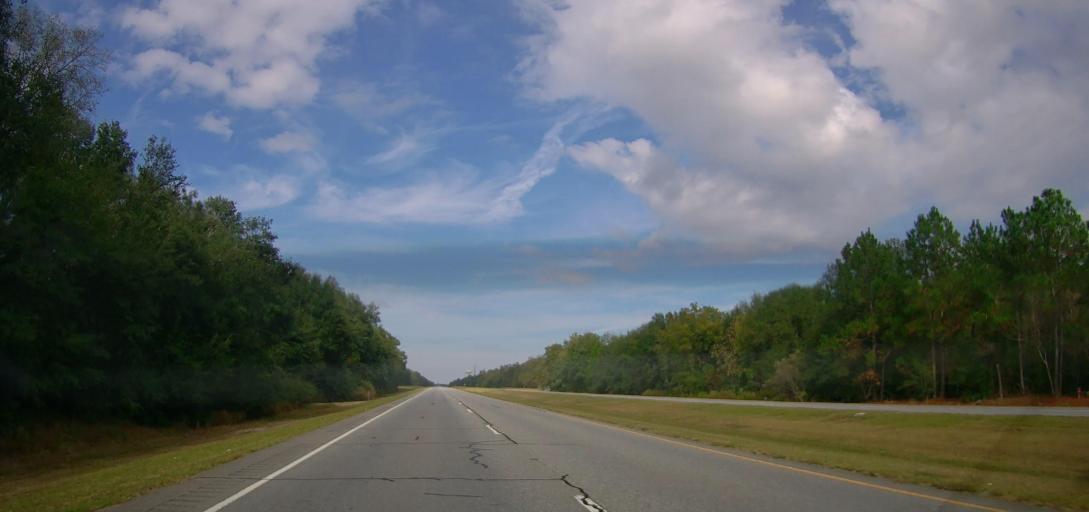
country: US
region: Georgia
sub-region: Mitchell County
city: Camilla
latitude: 31.2533
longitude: -84.1976
